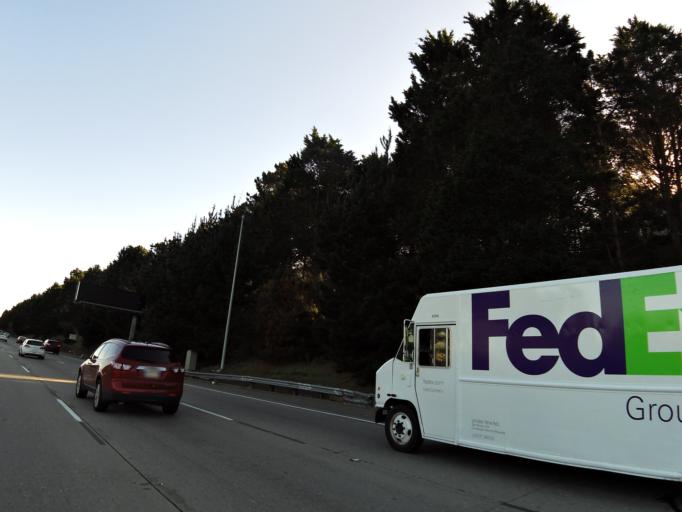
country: US
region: California
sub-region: San Mateo County
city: Colma
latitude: 37.6598
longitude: -122.4641
